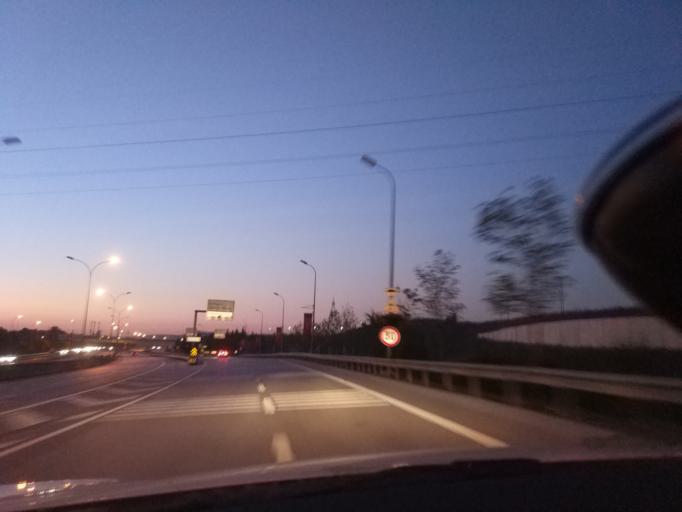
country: TR
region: Istanbul
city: Pendik
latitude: 40.9179
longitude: 29.3218
